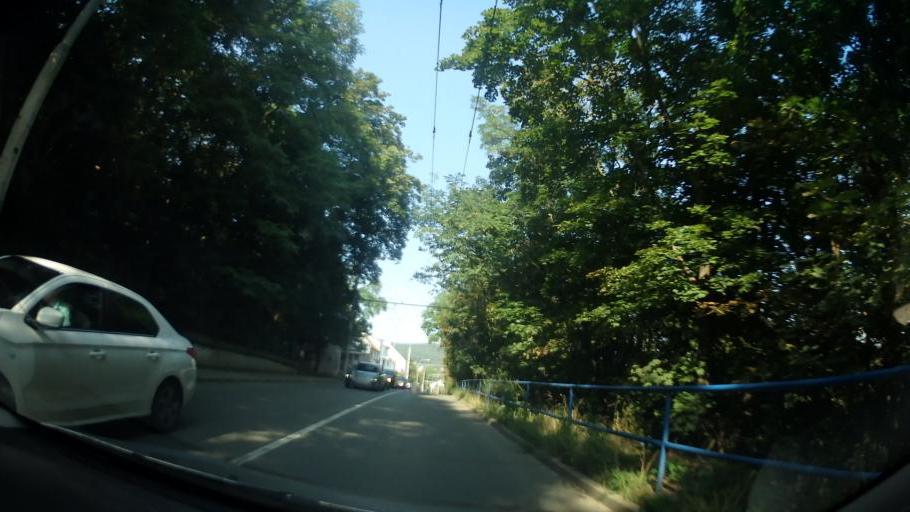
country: CZ
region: South Moravian
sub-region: Mesto Brno
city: Brno
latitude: 49.2035
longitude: 16.5628
